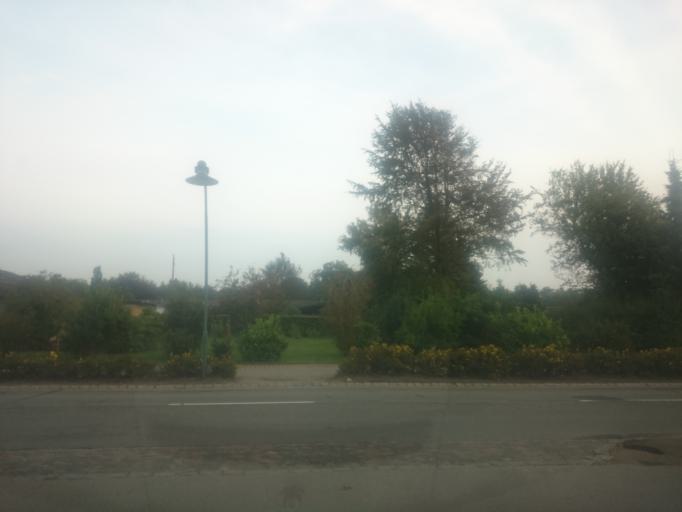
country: DK
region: South Denmark
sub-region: Billund Kommune
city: Billund
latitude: 55.7327
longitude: 9.1222
